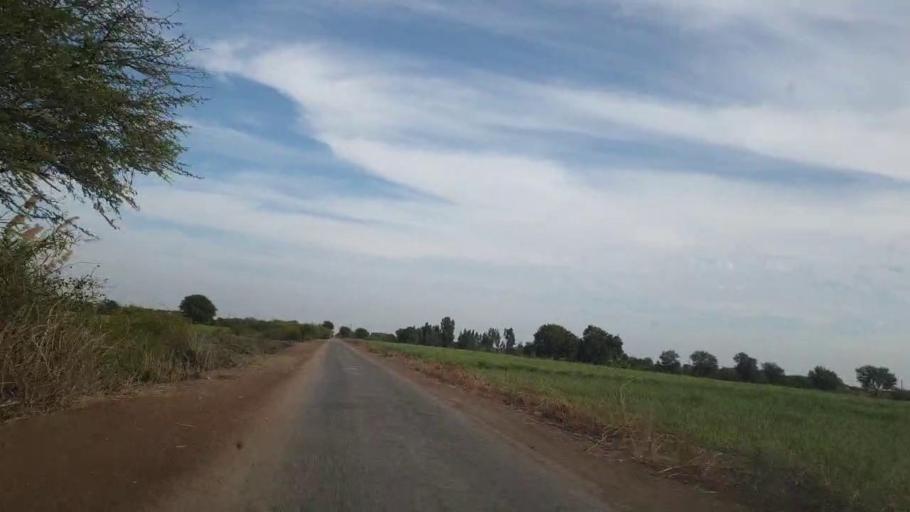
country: PK
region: Sindh
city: Pithoro
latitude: 25.6329
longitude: 69.4000
